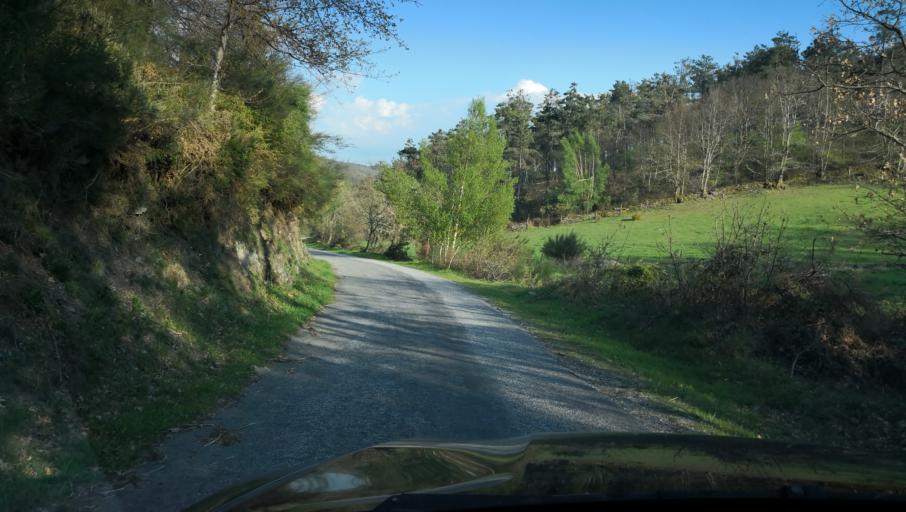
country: PT
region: Vila Real
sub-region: Vila Real
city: Vila Real
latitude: 41.3092
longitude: -7.8477
